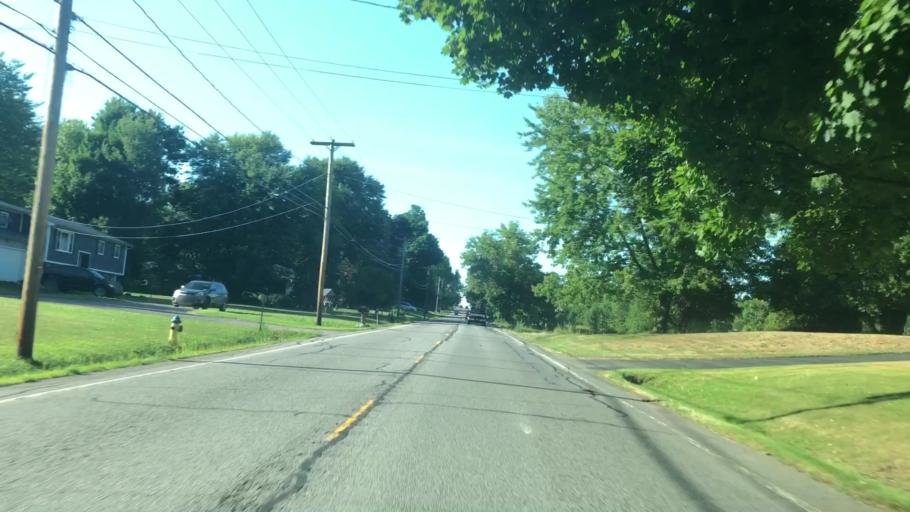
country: US
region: New York
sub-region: Wayne County
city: Macedon
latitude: 43.1442
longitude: -77.2926
